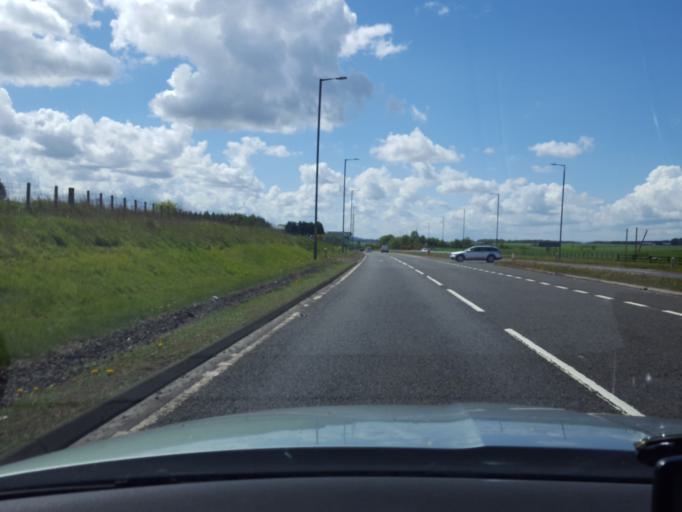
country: GB
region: Scotland
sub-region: Angus
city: Forfar
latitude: 56.6734
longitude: -2.8944
